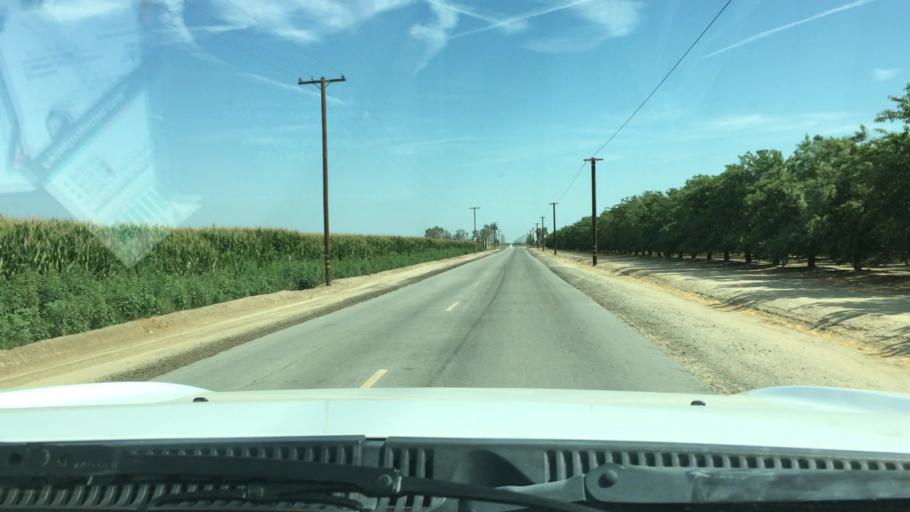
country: US
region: California
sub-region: Kern County
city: Buttonwillow
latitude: 35.4243
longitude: -119.3763
